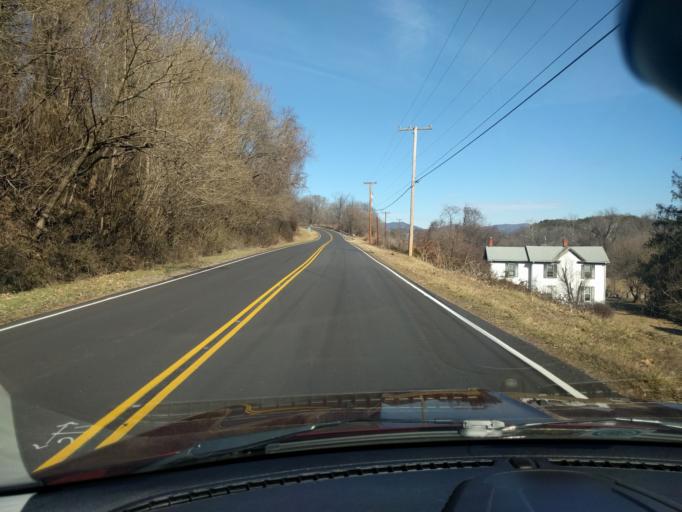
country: US
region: Virginia
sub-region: Botetourt County
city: Laymantown
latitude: 37.3247
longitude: -79.8677
